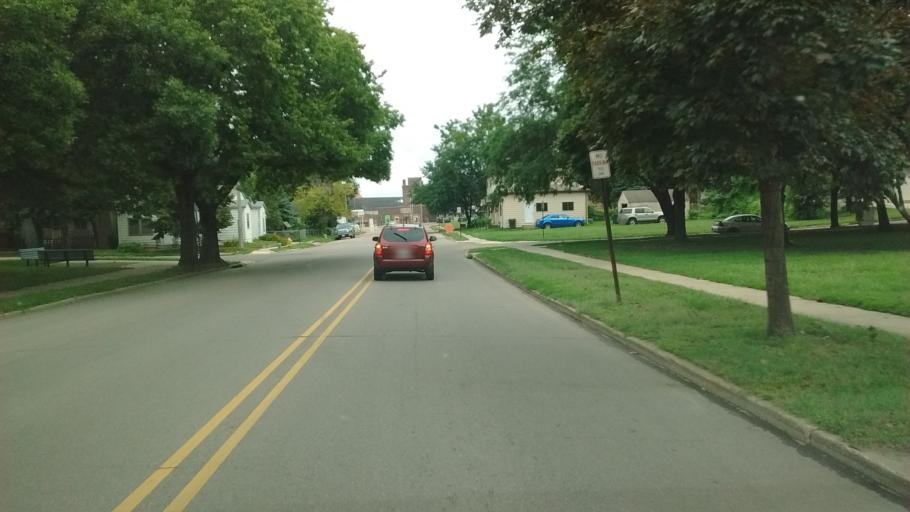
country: US
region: Iowa
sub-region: Woodbury County
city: Sioux City
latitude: 42.4977
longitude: -96.4151
